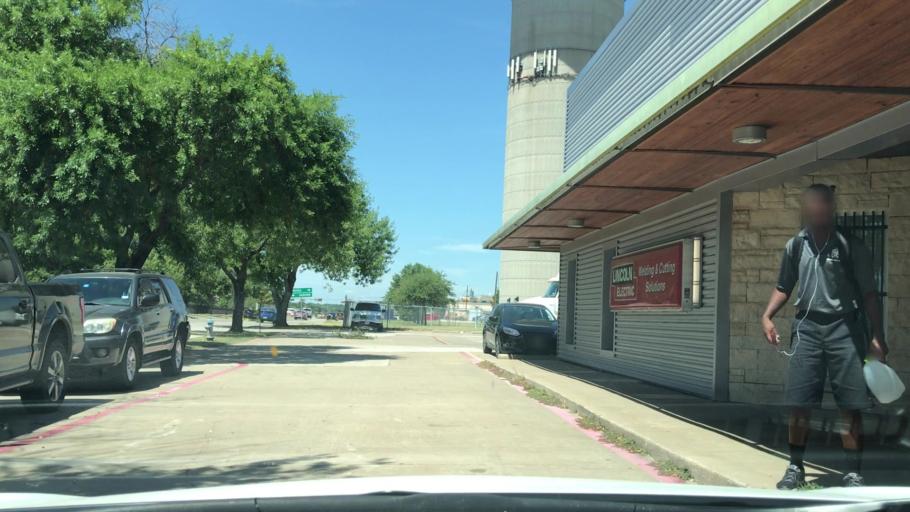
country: US
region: Texas
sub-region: Collin County
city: McKinney
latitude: 33.1799
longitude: -96.6158
